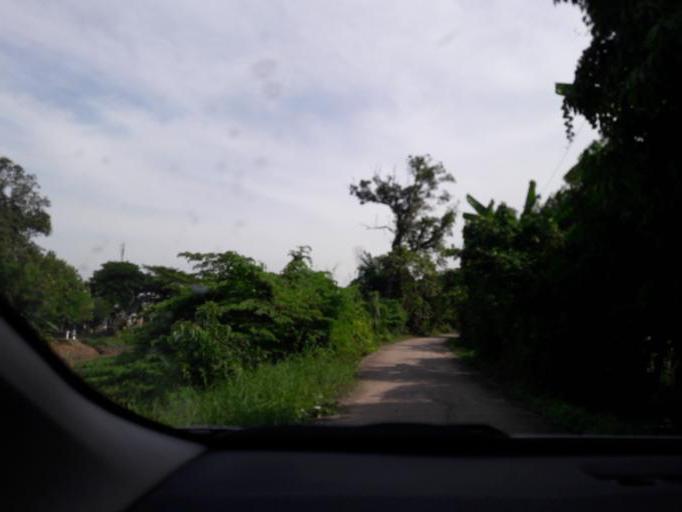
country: TH
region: Ang Thong
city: Ang Thong
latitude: 14.5808
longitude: 100.4409
